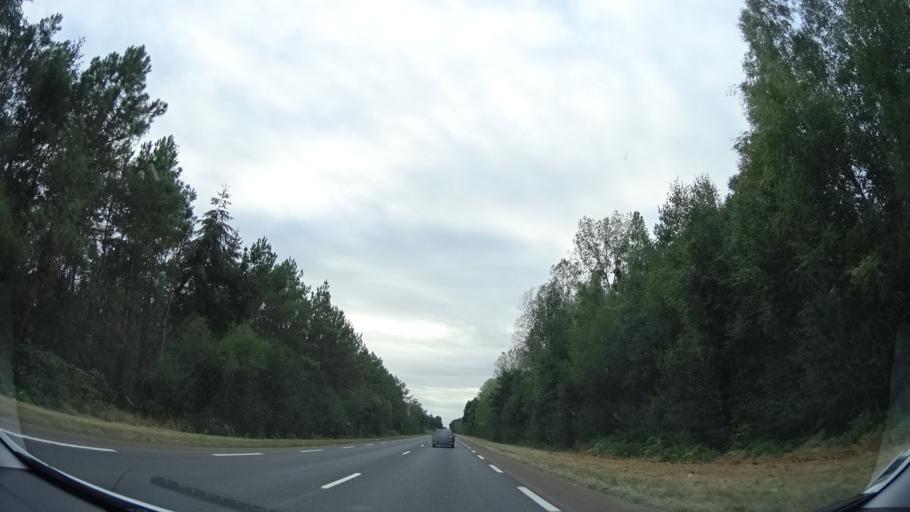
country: FR
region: Pays de la Loire
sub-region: Departement de la Sarthe
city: Saint-Mars-la-Briere
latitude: 48.0052
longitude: 0.3692
